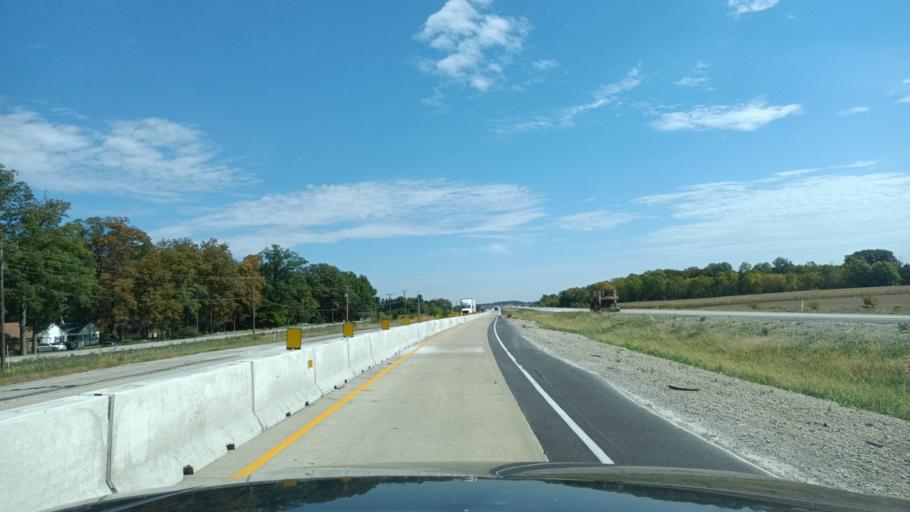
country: US
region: Indiana
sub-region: Allen County
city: New Haven
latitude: 41.1075
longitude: -84.9557
